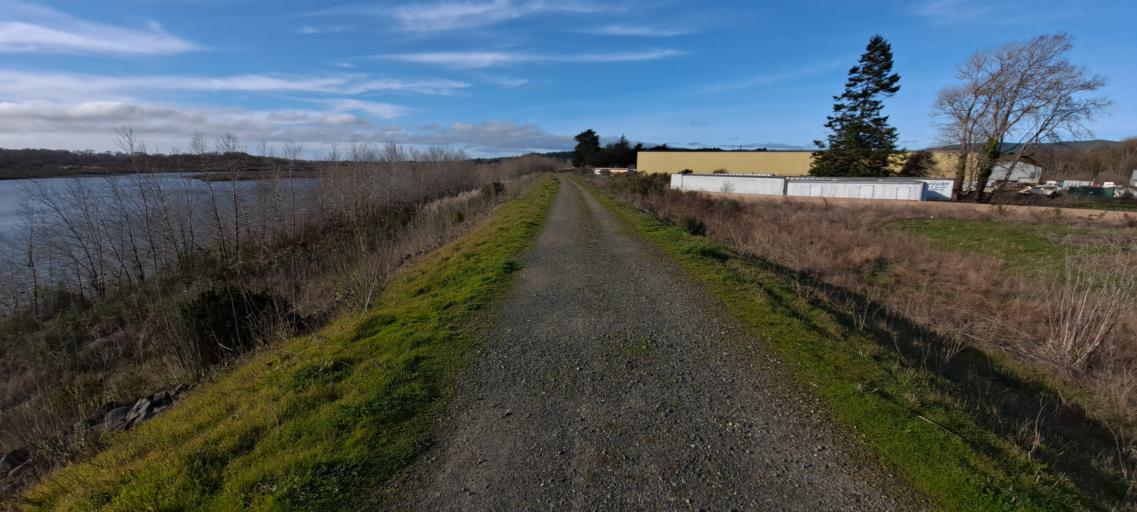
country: US
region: California
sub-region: Humboldt County
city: Fortuna
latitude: 40.5836
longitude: -124.1580
